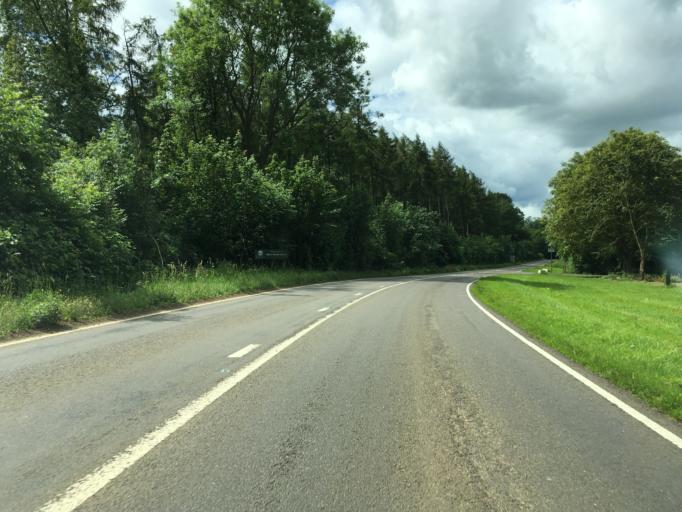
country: GB
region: England
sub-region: Oxfordshire
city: Hook Norton
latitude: 51.9844
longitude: -1.4268
